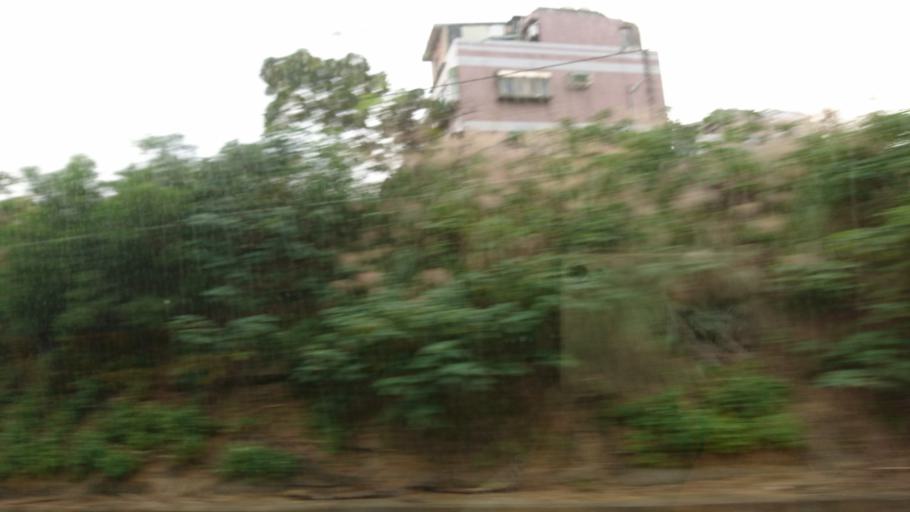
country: TW
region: Taiwan
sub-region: Hsinchu
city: Zhubei
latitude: 24.8624
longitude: 120.9935
